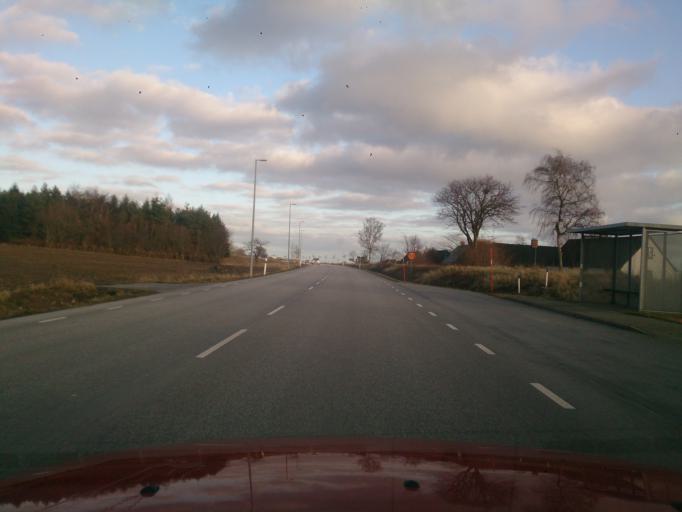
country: SE
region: Skane
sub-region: Ystads Kommun
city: Ystad
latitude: 55.4268
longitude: 13.7246
